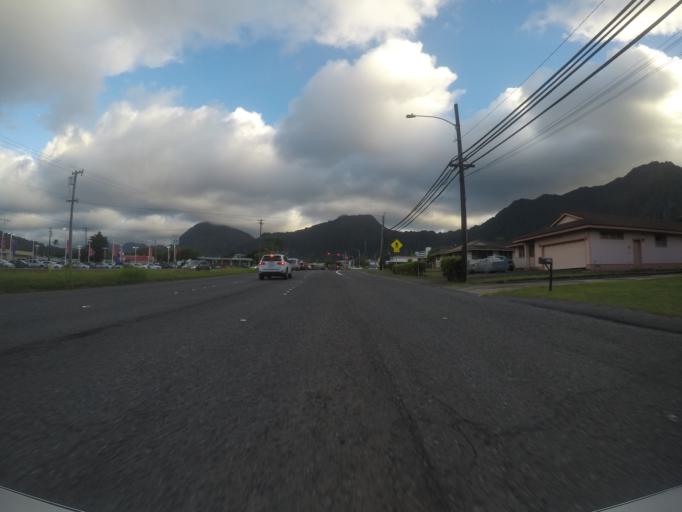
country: US
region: Hawaii
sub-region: Honolulu County
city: Kane'ohe
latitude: 21.4039
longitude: -157.7995
